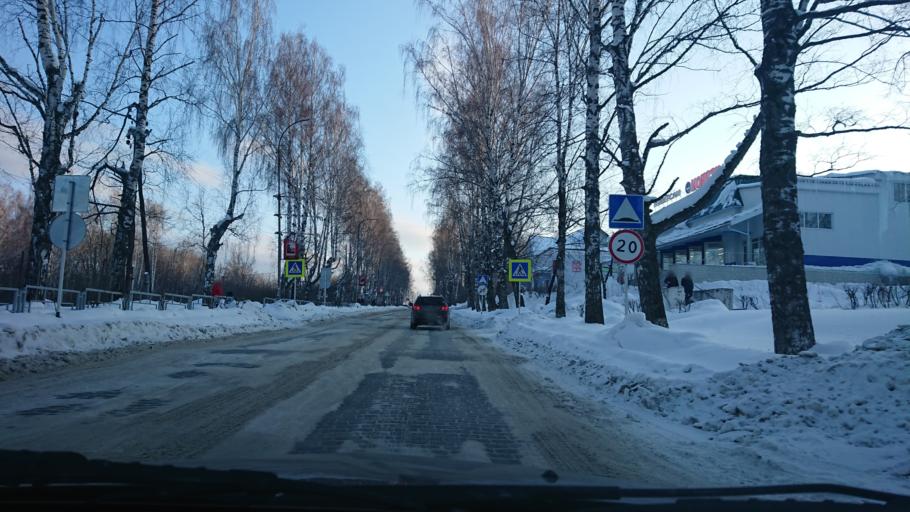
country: RU
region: Sverdlovsk
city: Degtyarsk
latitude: 56.6958
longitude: 60.0884
